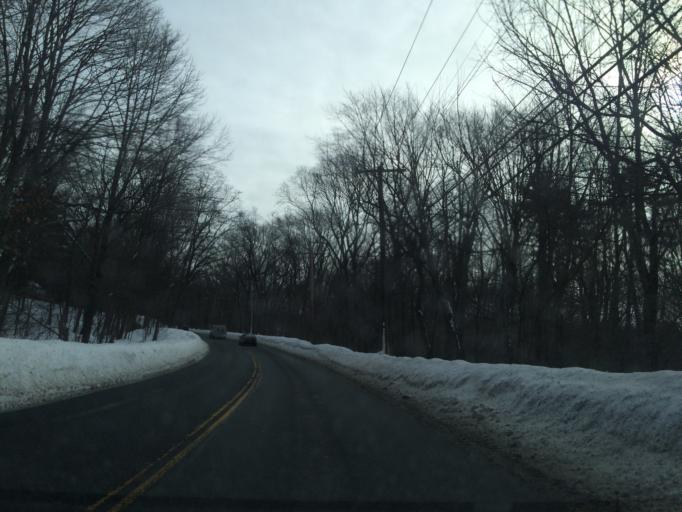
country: US
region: Massachusetts
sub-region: Middlesex County
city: Weston
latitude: 42.3418
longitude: -71.3016
